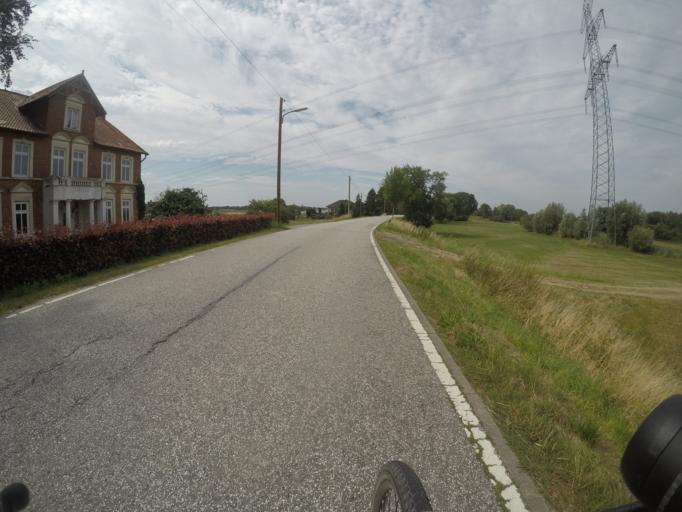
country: DE
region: Schleswig-Holstein
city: Oststeinbek
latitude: 53.4697
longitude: 10.1400
